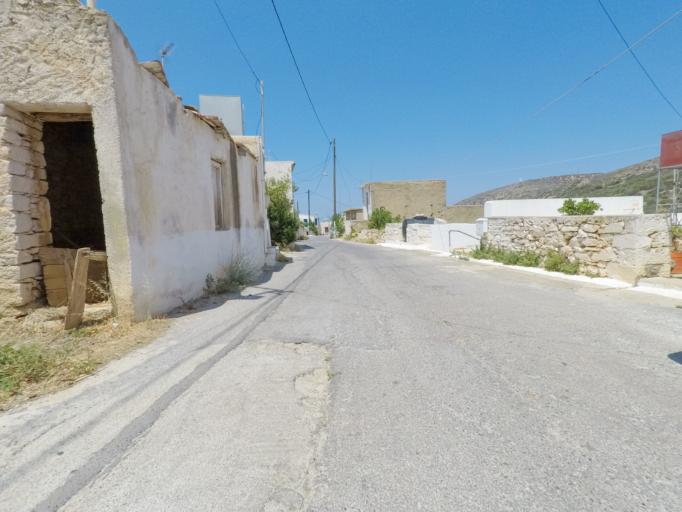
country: GR
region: Crete
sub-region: Nomos Lasithiou
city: Elounda
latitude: 35.3160
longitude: 25.7340
